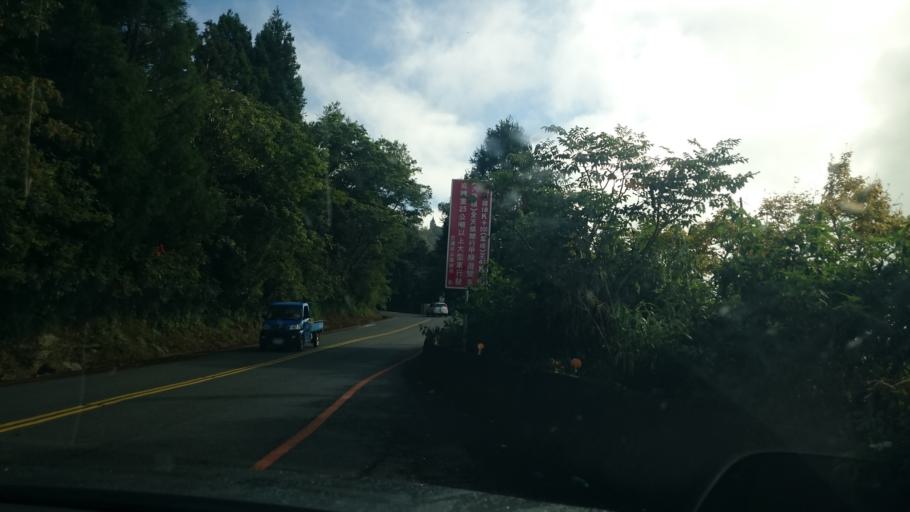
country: TW
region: Taiwan
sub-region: Nantou
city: Puli
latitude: 24.0586
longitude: 121.1646
